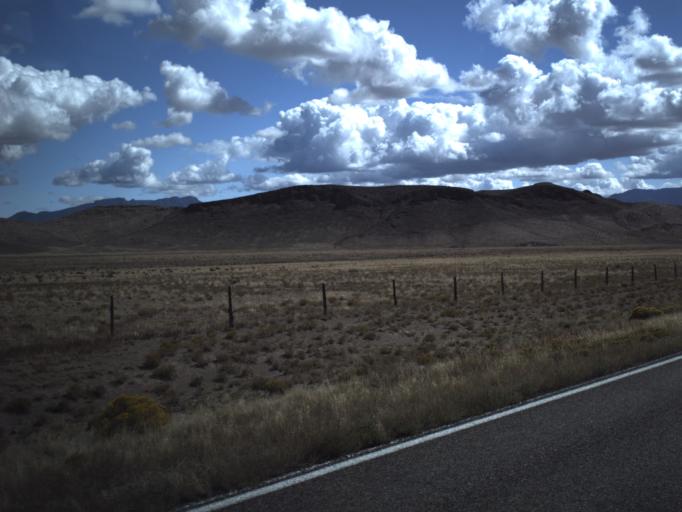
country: US
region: Utah
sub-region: Beaver County
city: Milford
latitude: 38.5997
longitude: -113.8302
